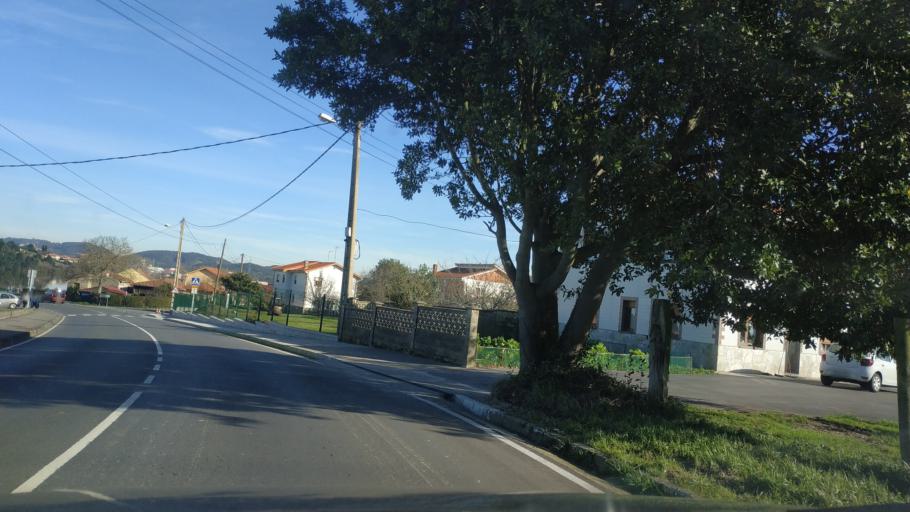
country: ES
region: Asturias
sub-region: Province of Asturias
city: Corvera de Asturias
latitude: 43.5392
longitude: -5.8819
